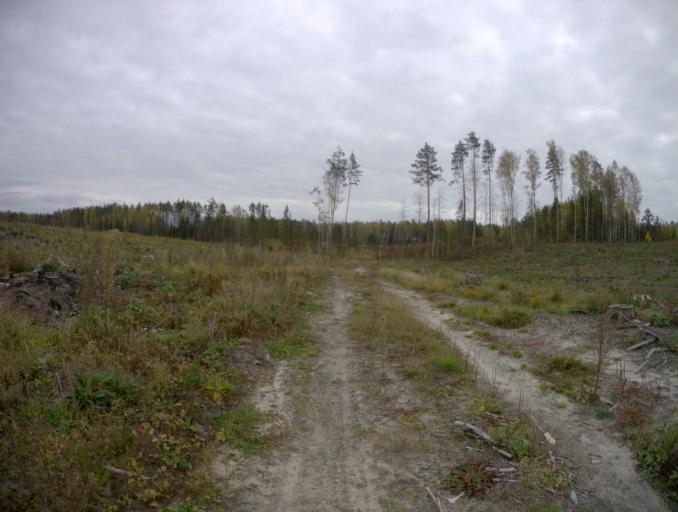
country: RU
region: Vladimir
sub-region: Kovrovskiy Rayon
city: Kovrov
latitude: 56.3145
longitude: 41.5149
